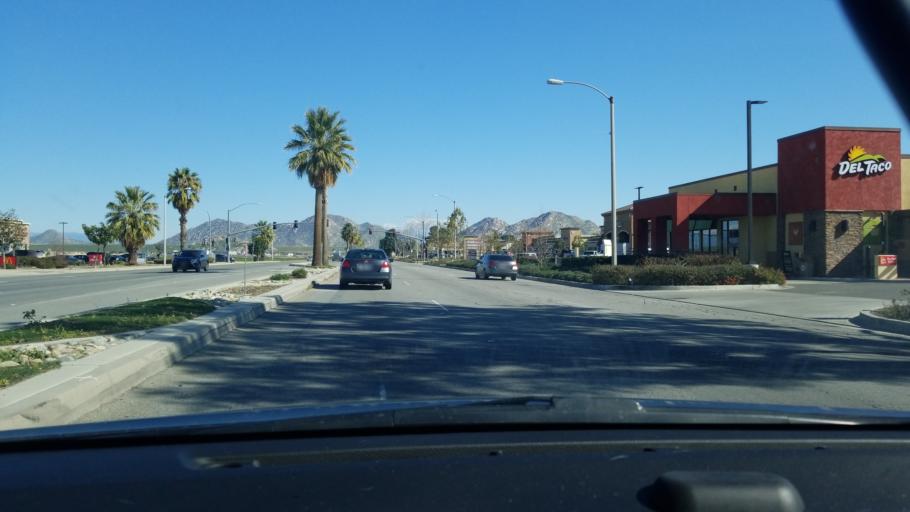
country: US
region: California
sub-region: Riverside County
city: March Air Force Base
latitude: 33.8445
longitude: -117.2254
